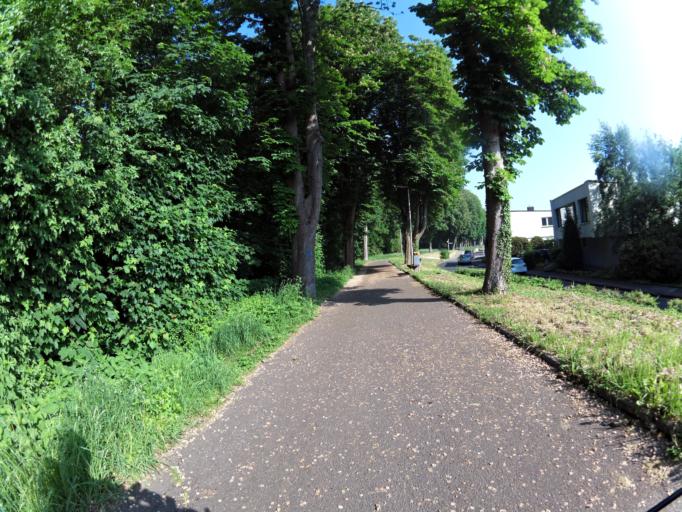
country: DE
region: North Rhine-Westphalia
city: Julich
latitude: 50.9143
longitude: 6.3539
